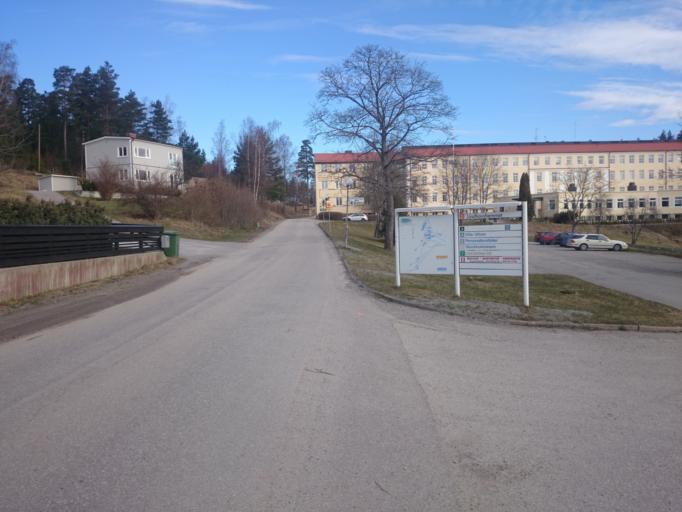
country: SE
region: Stockholm
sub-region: Botkyrka Kommun
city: Tumba
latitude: 59.2002
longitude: 17.8029
